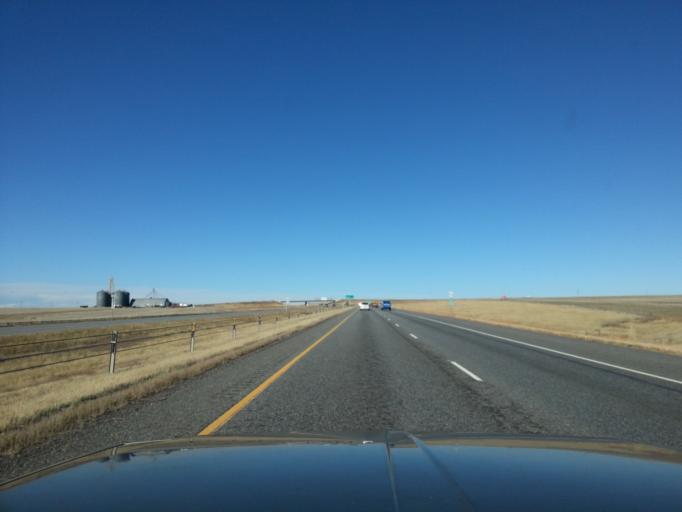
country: US
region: Colorado
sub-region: Adams County
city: Aurora
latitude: 39.8494
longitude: -104.7467
